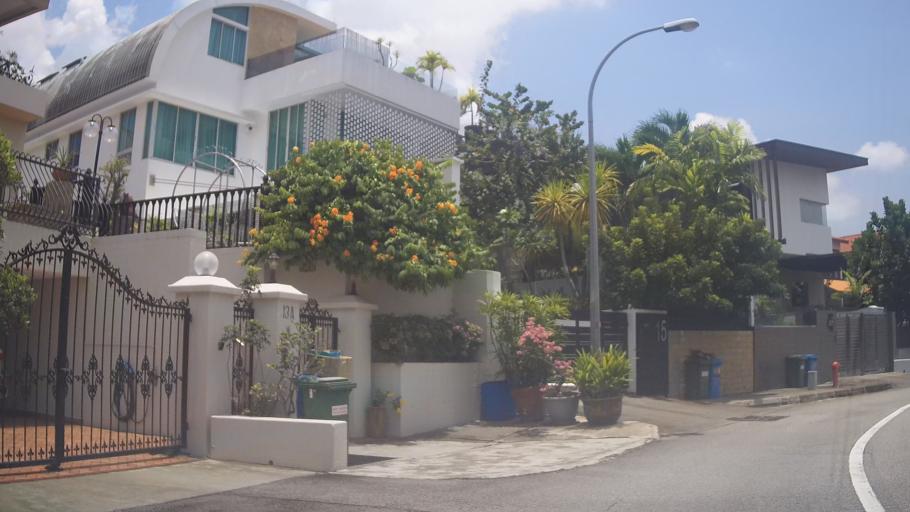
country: SG
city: Singapore
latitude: 1.3620
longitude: 103.8722
